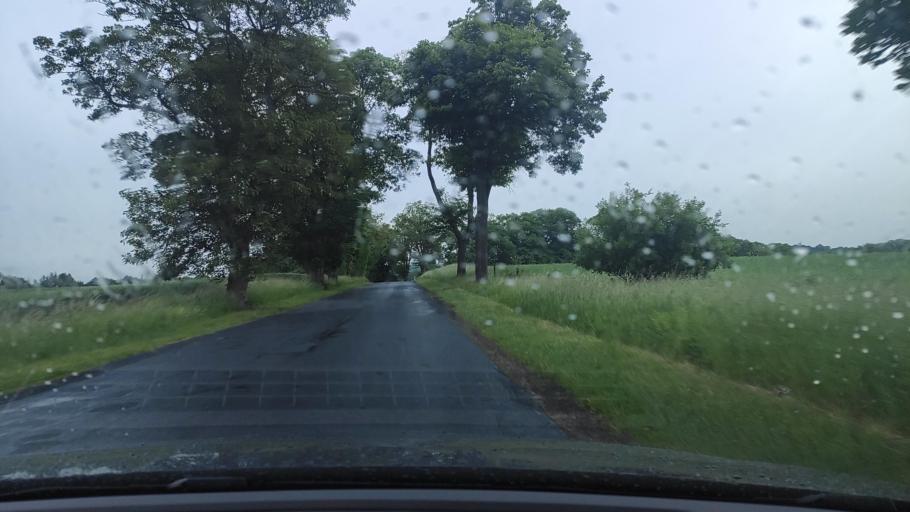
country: PL
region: Greater Poland Voivodeship
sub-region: Powiat poznanski
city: Kobylnica
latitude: 52.4830
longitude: 17.0940
